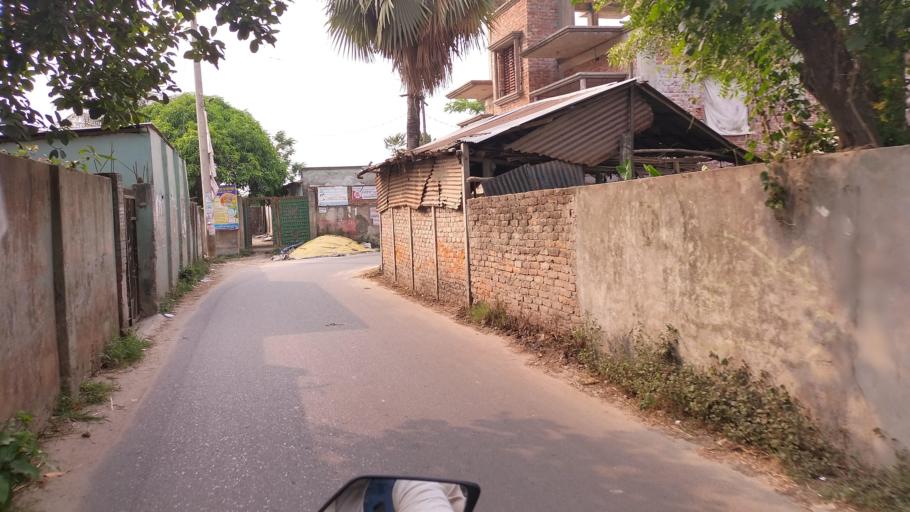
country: BD
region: Dhaka
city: Azimpur
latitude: 23.6675
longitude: 90.3480
